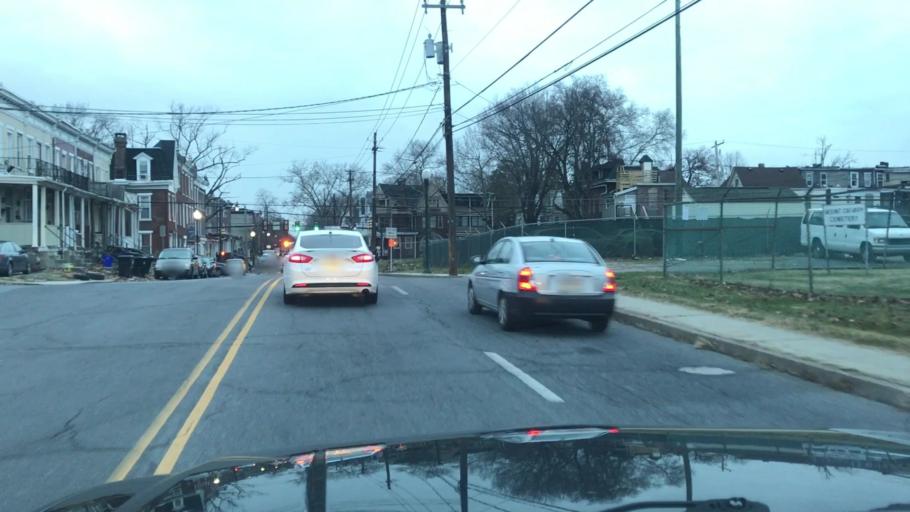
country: US
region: Pennsylvania
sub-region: Dauphin County
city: Harrisburg
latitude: 40.2581
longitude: -76.8665
